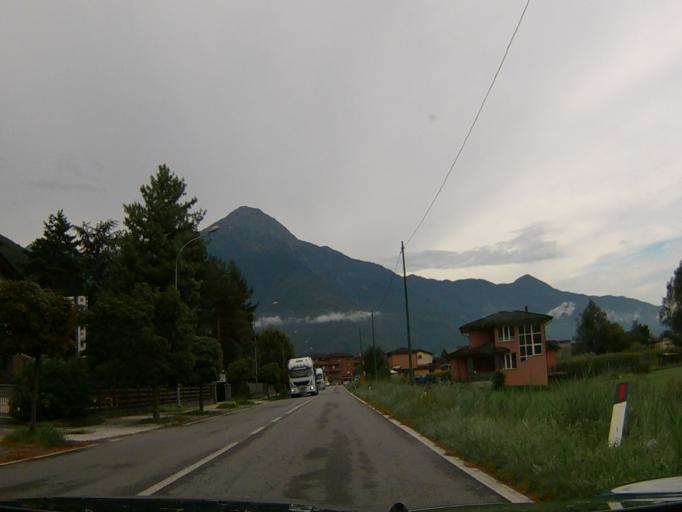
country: IT
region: Lombardy
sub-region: Provincia di Sondrio
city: Dubino
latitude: 46.1740
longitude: 9.4341
